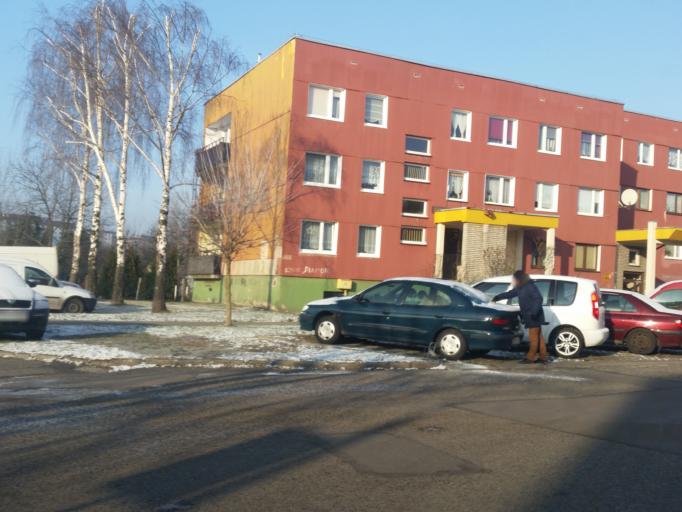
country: PL
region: Silesian Voivodeship
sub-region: Sosnowiec
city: Sosnowiec
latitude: 50.2712
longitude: 19.1179
